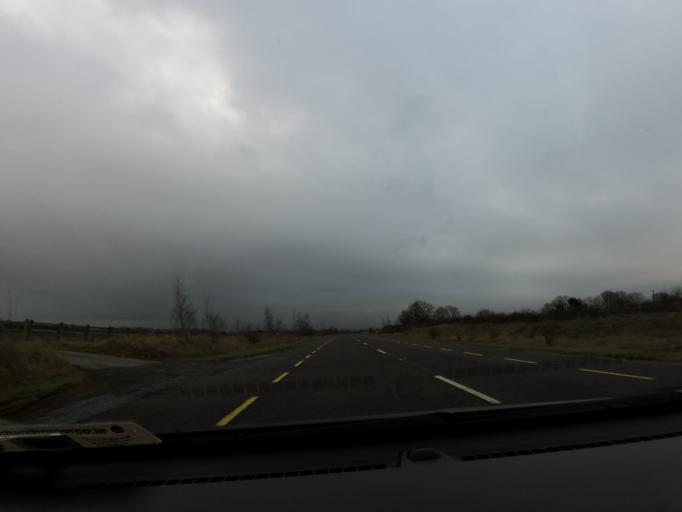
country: IE
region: Connaught
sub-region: County Galway
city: Loughrea
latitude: 53.2466
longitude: -8.5939
